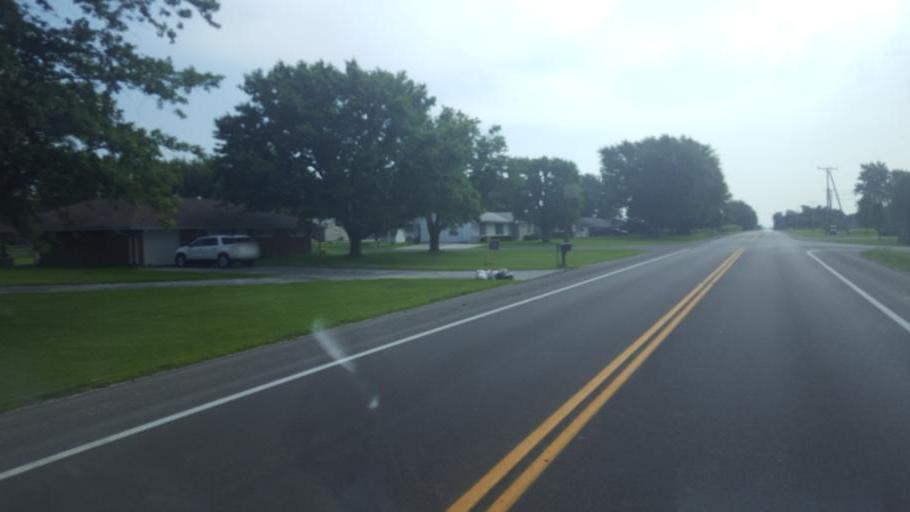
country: US
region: Ohio
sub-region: Hardin County
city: Kenton
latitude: 40.6445
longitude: -83.5790
